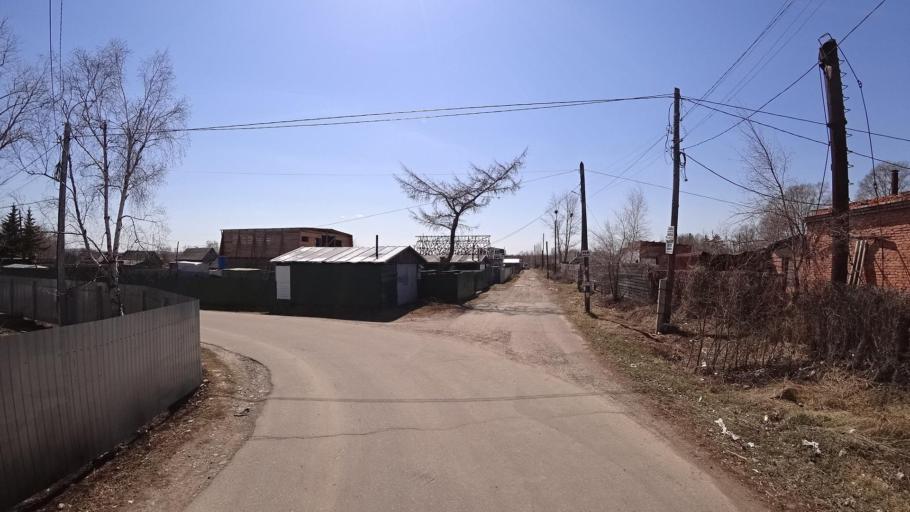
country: RU
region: Khabarovsk Krai
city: Khurba
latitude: 50.4064
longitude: 136.8835
